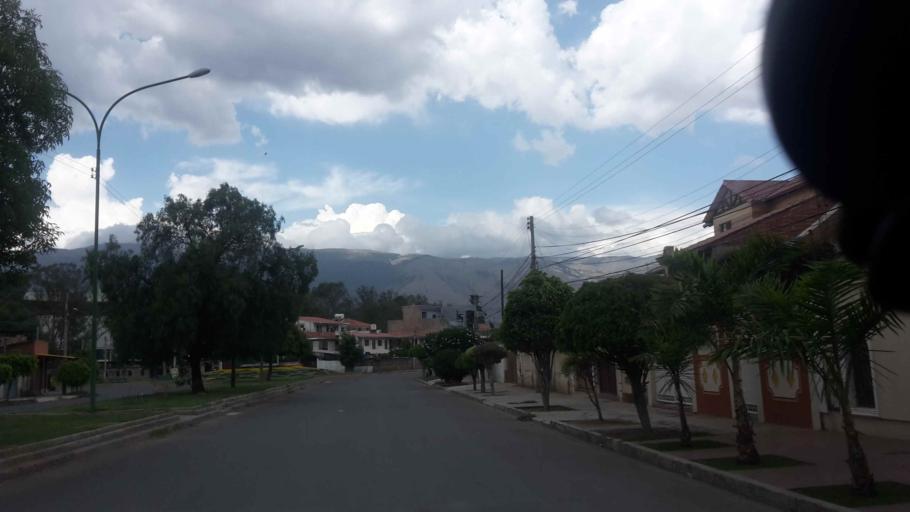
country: BO
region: Cochabamba
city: Cochabamba
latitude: -17.4038
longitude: -66.1746
